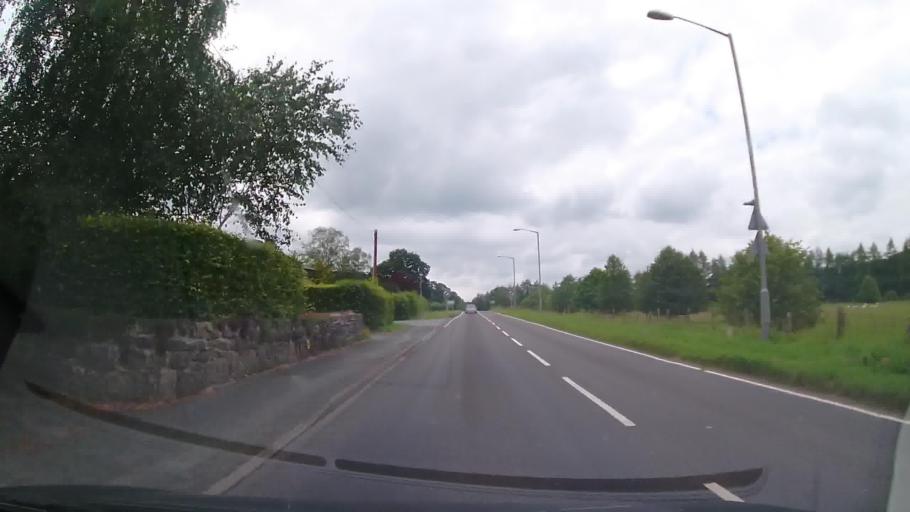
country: GB
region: Wales
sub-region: Gwynedd
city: Bala
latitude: 52.9151
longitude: -3.6025
